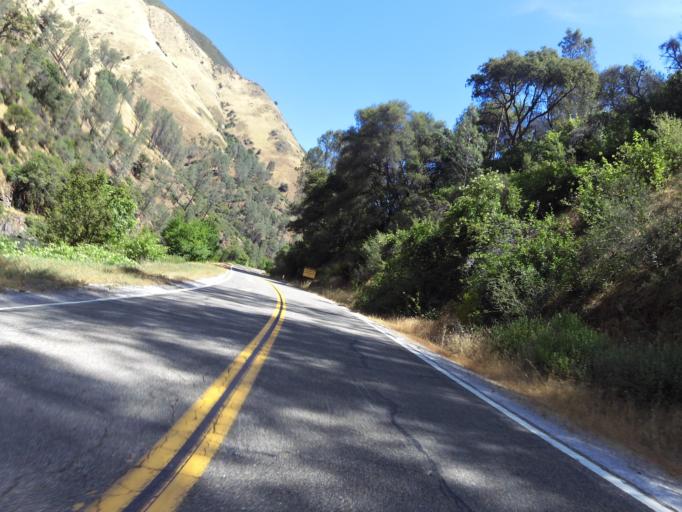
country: US
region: California
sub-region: Mariposa County
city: Midpines
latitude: 37.6401
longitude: -119.9265
